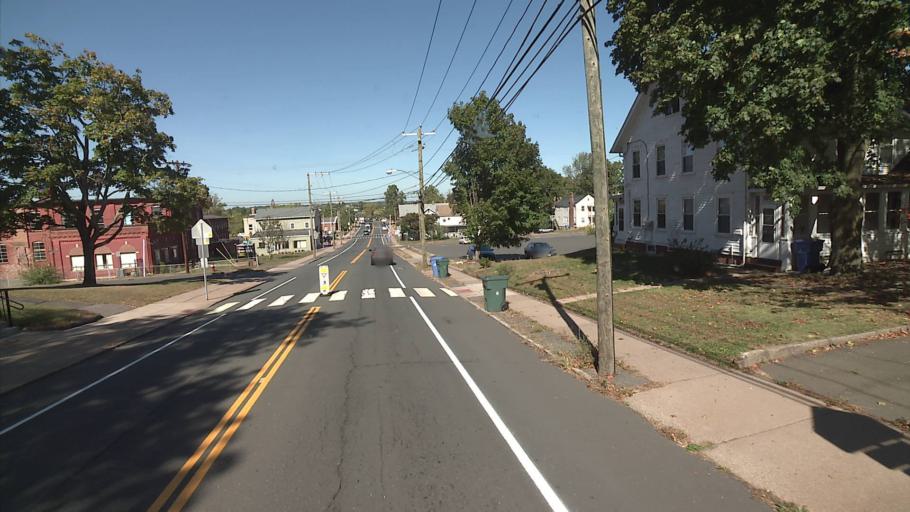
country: US
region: Connecticut
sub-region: Hartford County
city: Manchester
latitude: 41.7916
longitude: -72.5247
